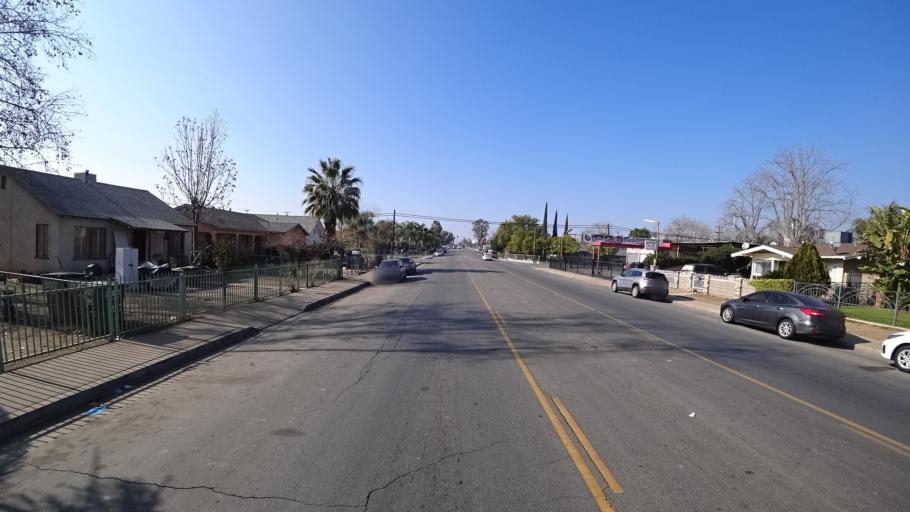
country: US
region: California
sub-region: Kern County
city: Bakersfield
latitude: 35.3846
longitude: -118.9828
